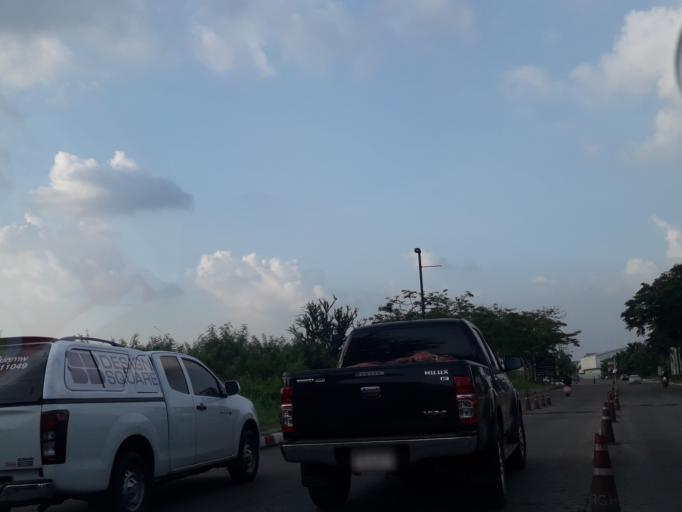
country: TH
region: Phra Nakhon Si Ayutthaya
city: Ban Bang Kadi Pathum Thani
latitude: 13.9933
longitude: 100.6176
